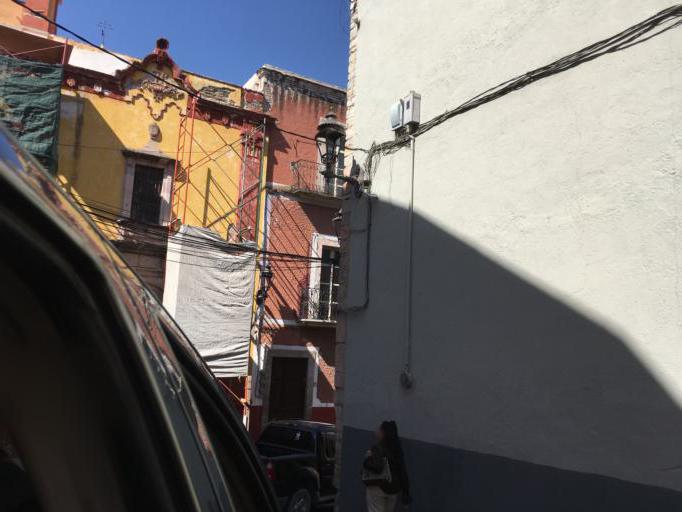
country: MX
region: Guanajuato
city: Guanajuato
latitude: 21.0171
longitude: -101.2521
